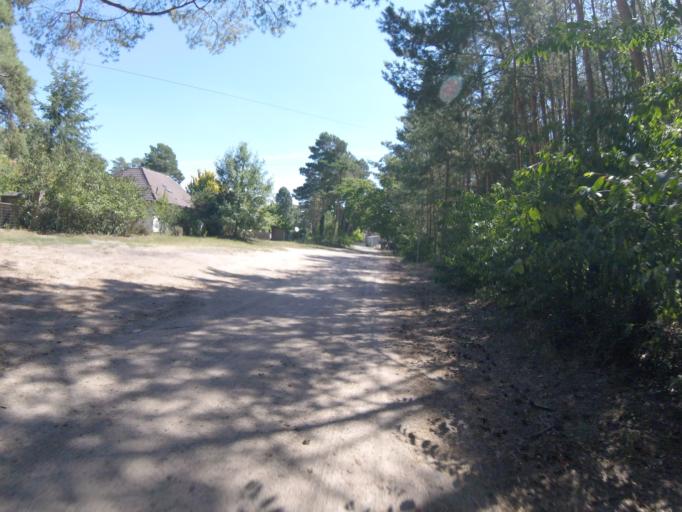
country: DE
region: Brandenburg
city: Bestensee
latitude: 52.2682
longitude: 13.6206
